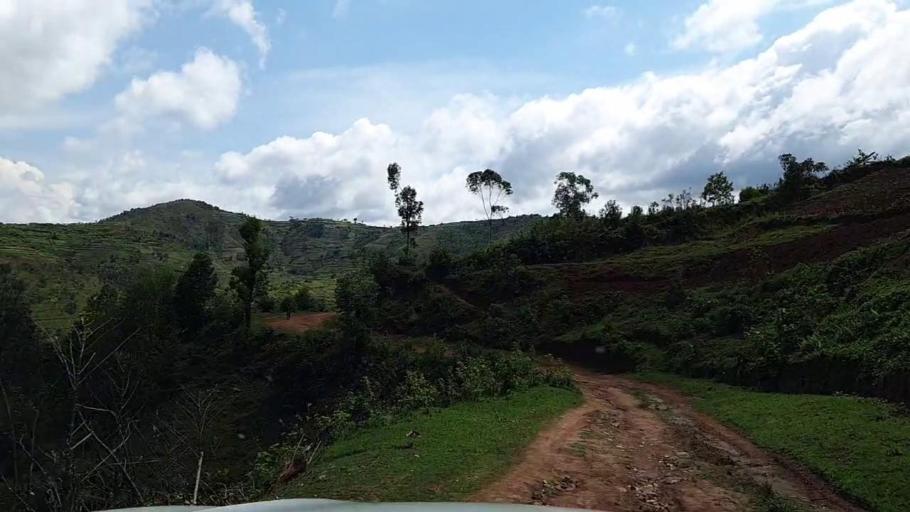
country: RW
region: Southern Province
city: Gikongoro
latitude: -2.3603
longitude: 29.5431
